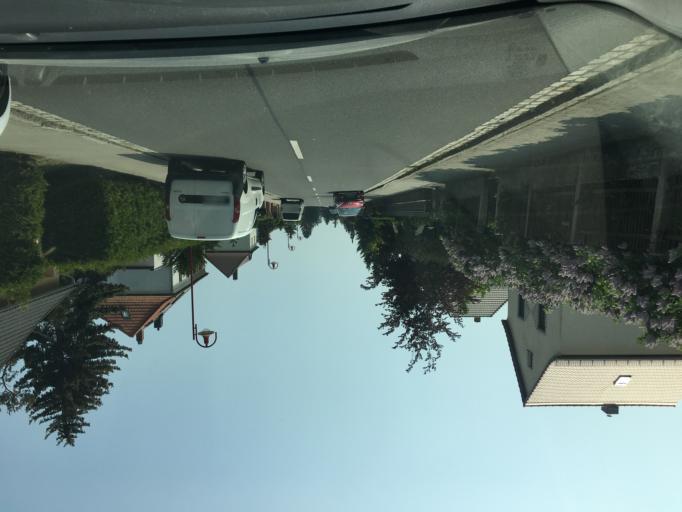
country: DE
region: Saxony
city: Grossposna
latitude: 51.2693
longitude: 12.4930
